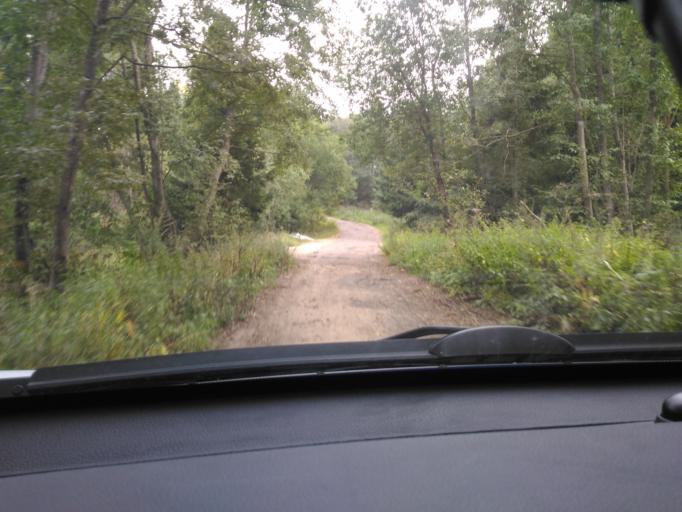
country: RU
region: Moskovskaya
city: Povarovo
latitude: 56.0930
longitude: 37.0578
